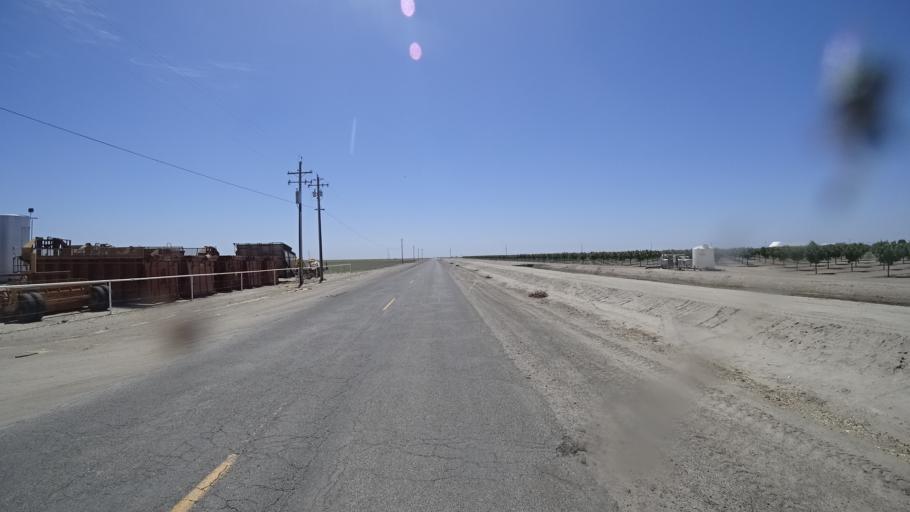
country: US
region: California
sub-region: Kings County
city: Corcoran
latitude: 36.1132
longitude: -119.6257
